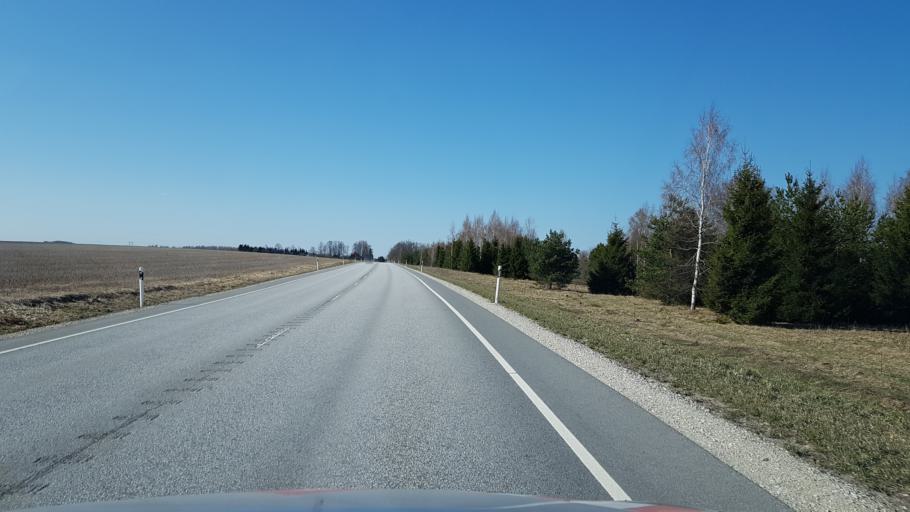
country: EE
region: Tartu
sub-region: Tartu linn
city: Tartu
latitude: 58.5391
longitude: 26.7646
